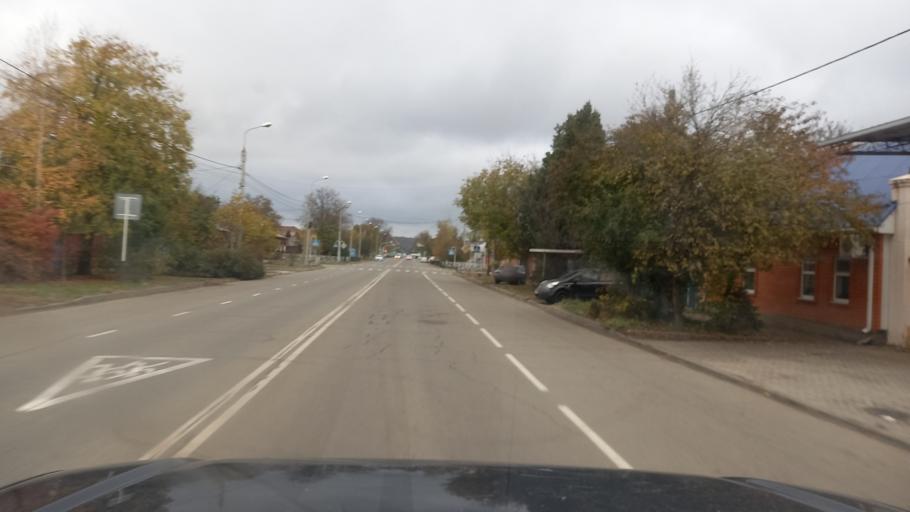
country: RU
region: Adygeya
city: Maykop
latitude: 44.6143
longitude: 40.1132
